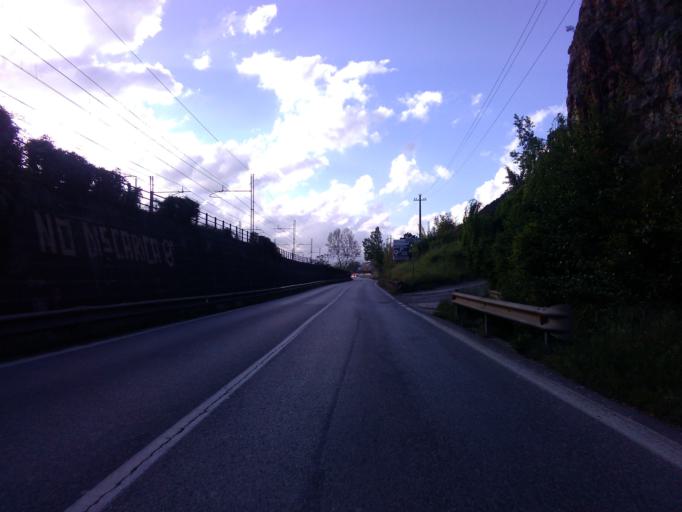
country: IT
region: Tuscany
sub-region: Provincia di Massa-Carrara
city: Capanne-Prato-Cinquale
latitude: 43.9972
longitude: 10.1730
